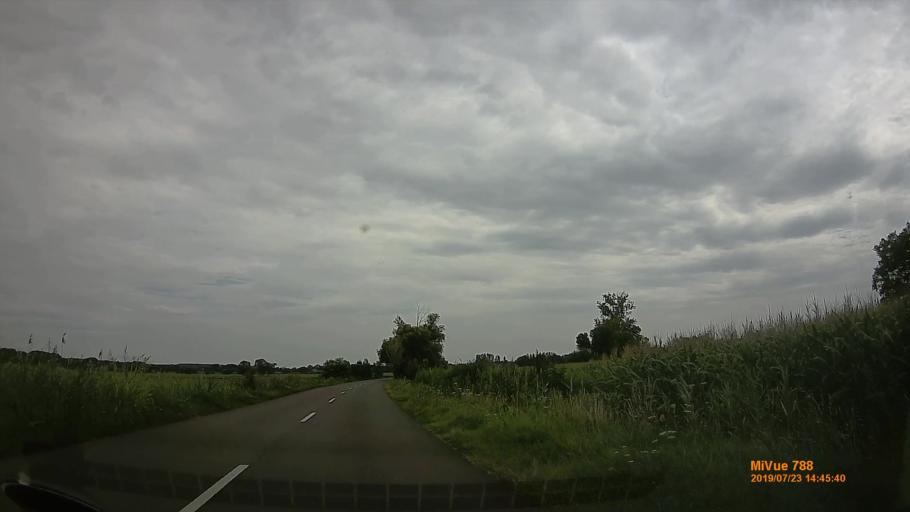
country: HU
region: Szabolcs-Szatmar-Bereg
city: Nyiregyhaza
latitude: 47.9268
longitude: 21.6772
